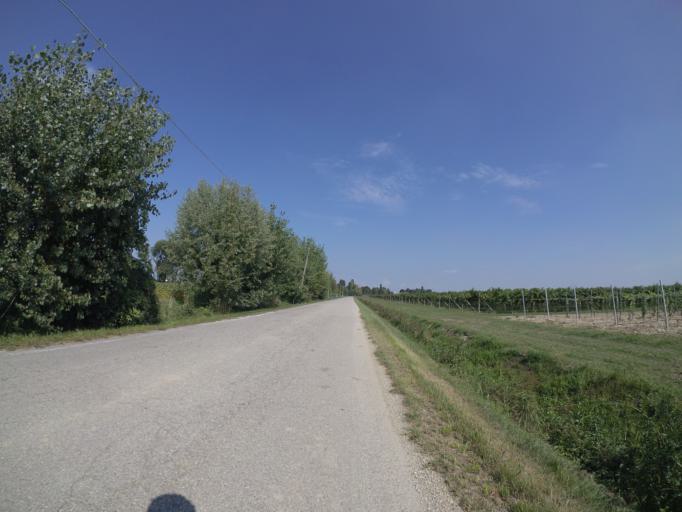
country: IT
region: Friuli Venezia Giulia
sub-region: Provincia di Udine
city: Camino al Tagliamento
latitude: 45.9208
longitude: 12.9353
